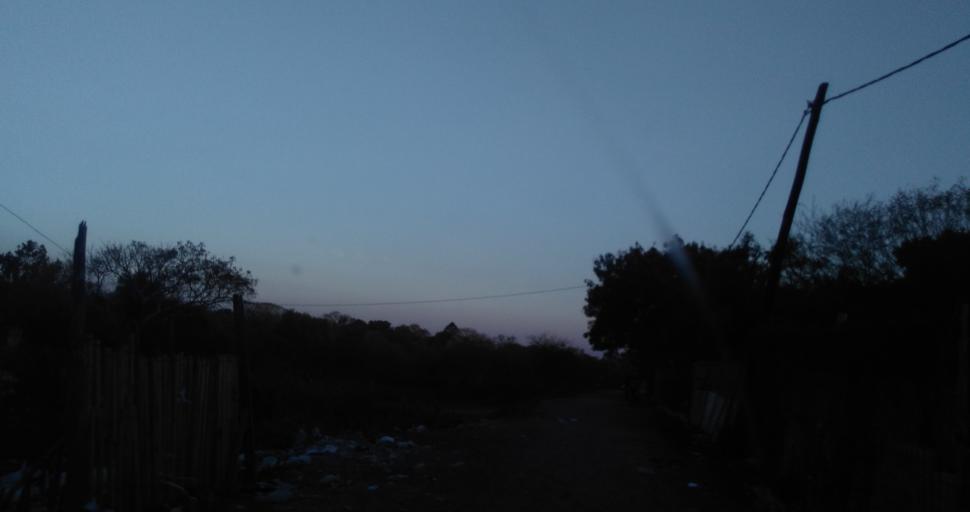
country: AR
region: Chaco
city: Resistencia
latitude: -27.4302
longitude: -58.9879
